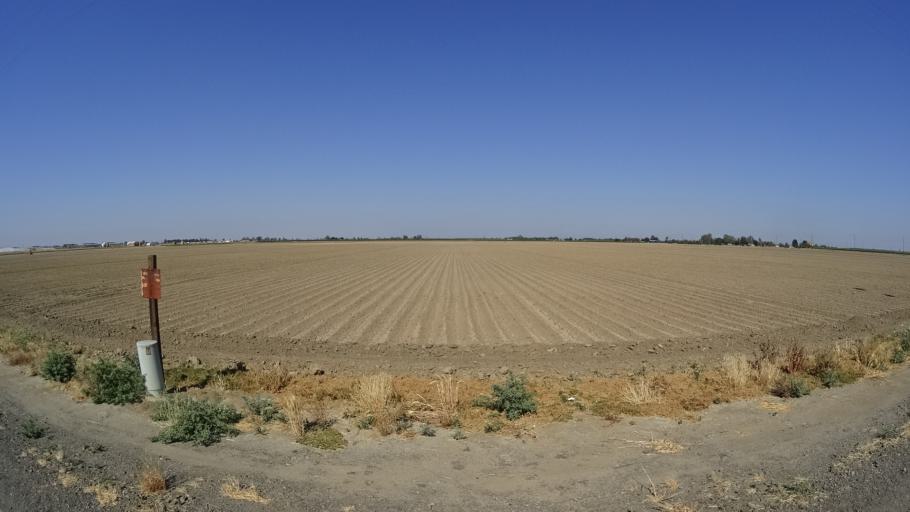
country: US
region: California
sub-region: Kings County
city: Home Garden
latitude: 36.3390
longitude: -119.5652
